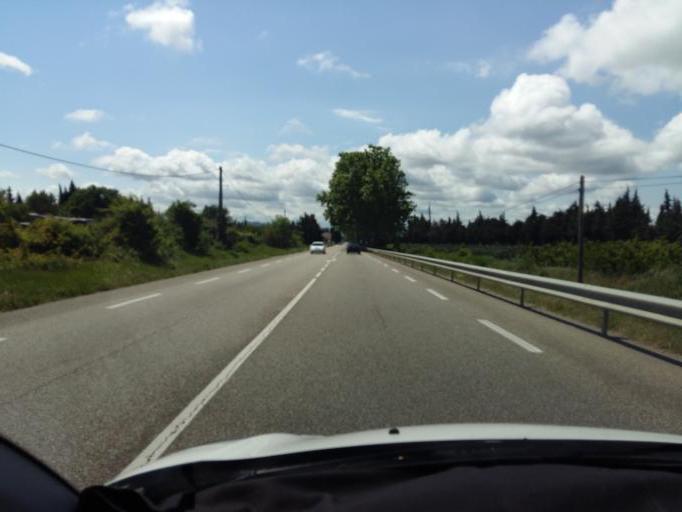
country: FR
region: Provence-Alpes-Cote d'Azur
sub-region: Departement des Bouches-du-Rhone
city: Senas
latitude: 43.7409
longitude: 5.1085
